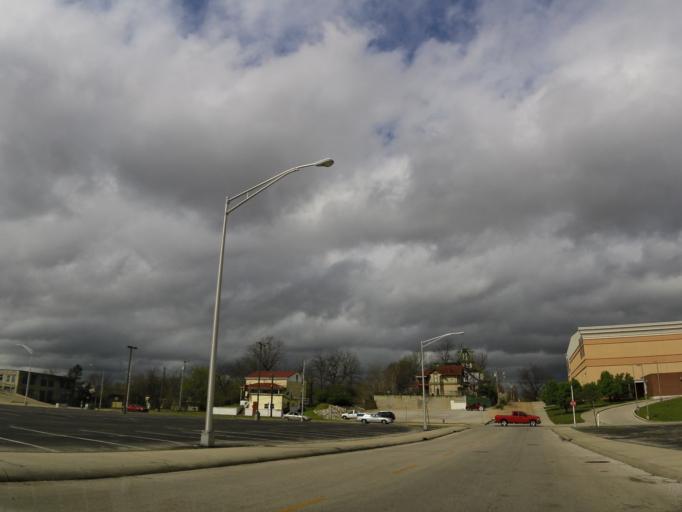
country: US
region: Missouri
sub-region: Butler County
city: Poplar Bluff
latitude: 36.7537
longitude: -90.3955
